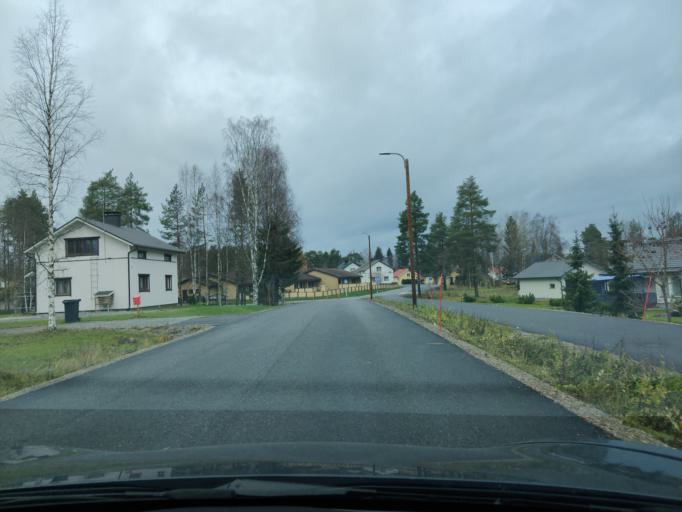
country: FI
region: Northern Savo
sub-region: Ylae-Savo
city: Kiuruvesi
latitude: 63.6481
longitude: 26.6369
